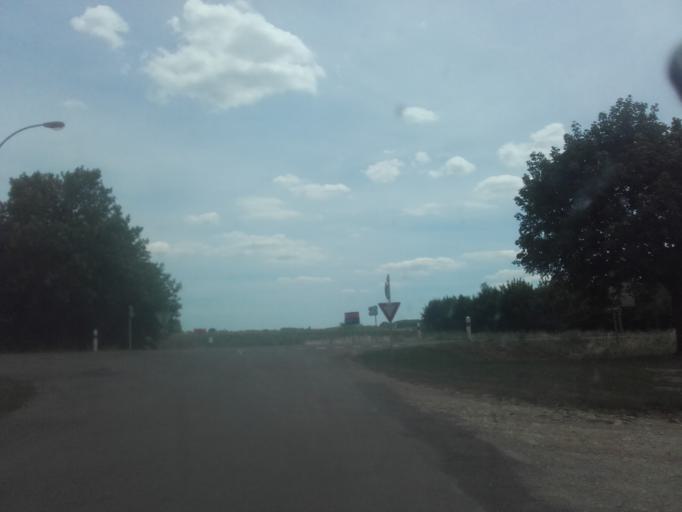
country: FR
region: Bourgogne
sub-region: Departement de la Cote-d'Or
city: Corpeau
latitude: 46.9243
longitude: 4.7375
